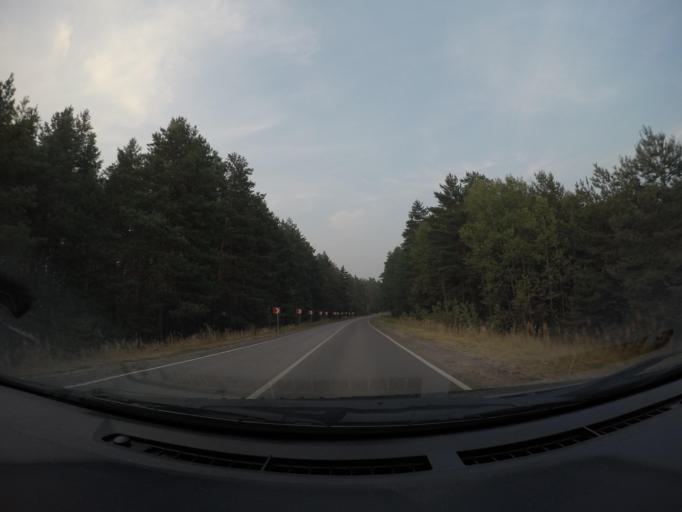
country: RU
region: Moskovskaya
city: Imeni Tsyurupy
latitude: 55.4941
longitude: 38.6826
